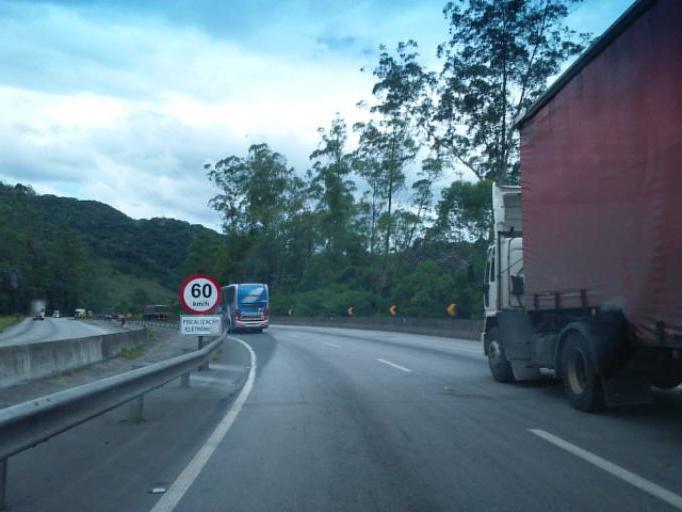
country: BR
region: Sao Paulo
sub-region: Juquitiba
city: Juquitiba
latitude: -24.0391
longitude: -47.1930
